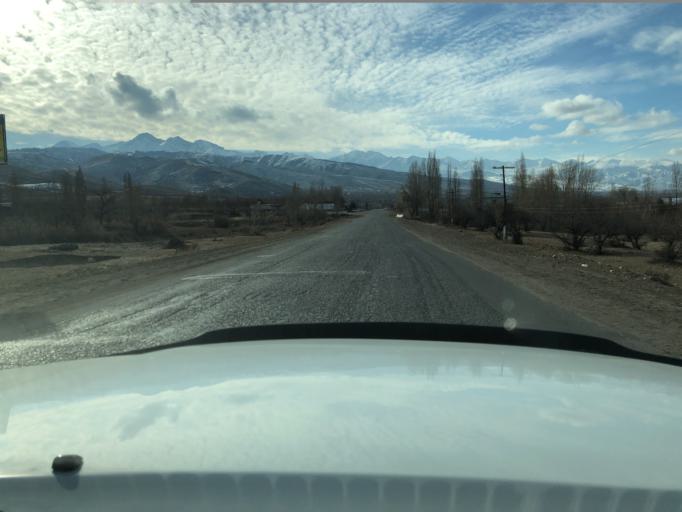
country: KG
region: Ysyk-Koel
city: Pokrovka
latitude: 42.2257
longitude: 77.7130
